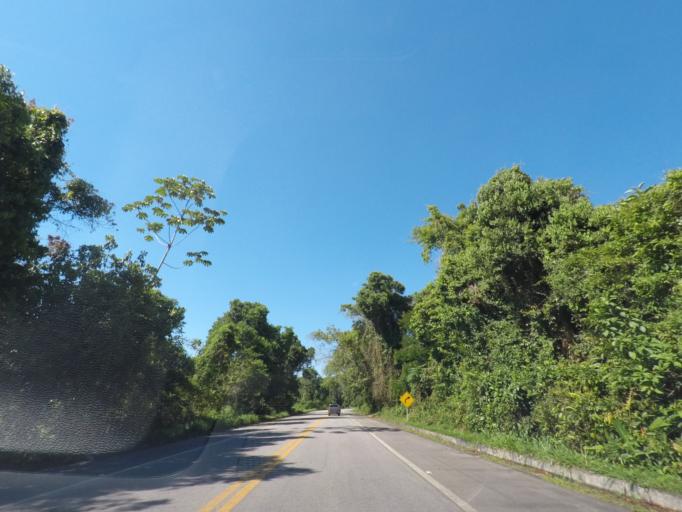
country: BR
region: Sao Paulo
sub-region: Ubatuba
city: Ubatuba
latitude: -23.3402
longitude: -44.9362
